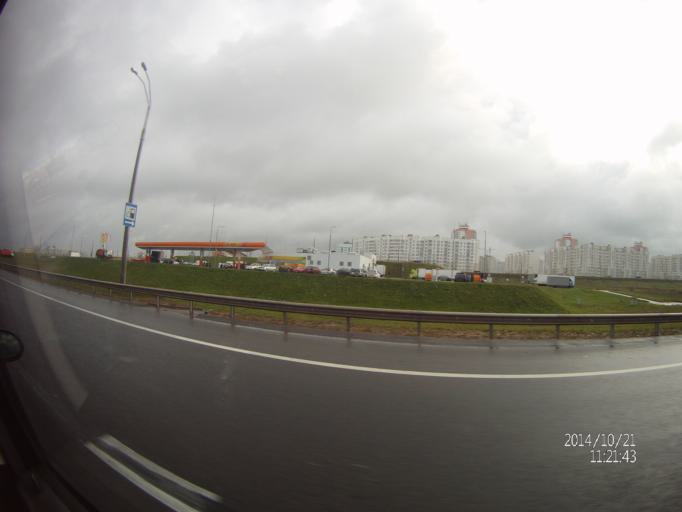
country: BY
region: Minsk
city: Zhdanovichy
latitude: 53.9163
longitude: 27.4124
